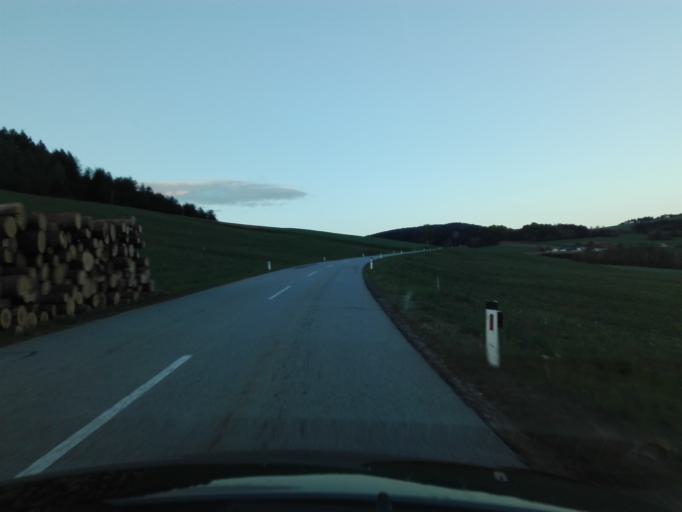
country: DE
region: Bavaria
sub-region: Lower Bavaria
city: Wegscheid
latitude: 48.5502
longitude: 13.7904
